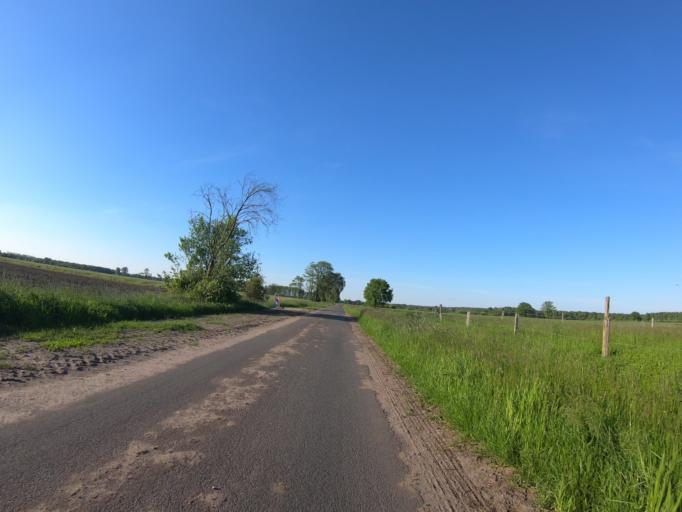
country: DE
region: Lower Saxony
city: Wagenhoff
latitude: 52.5320
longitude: 10.5624
